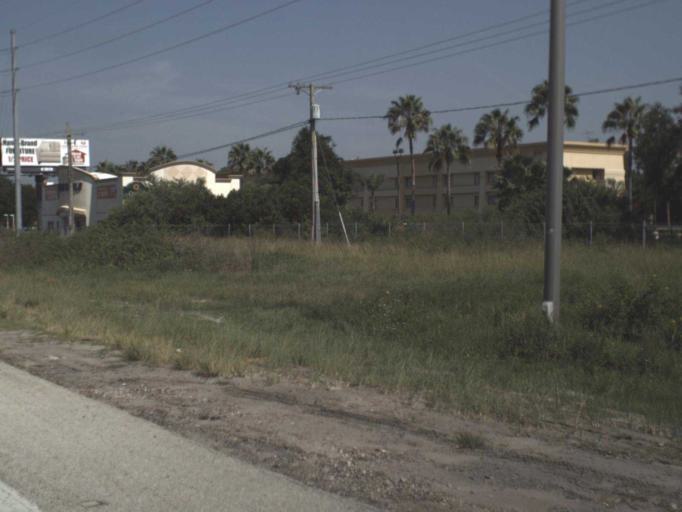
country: US
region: Florida
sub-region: Hillsborough County
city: Mango
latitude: 27.9434
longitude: -82.3334
